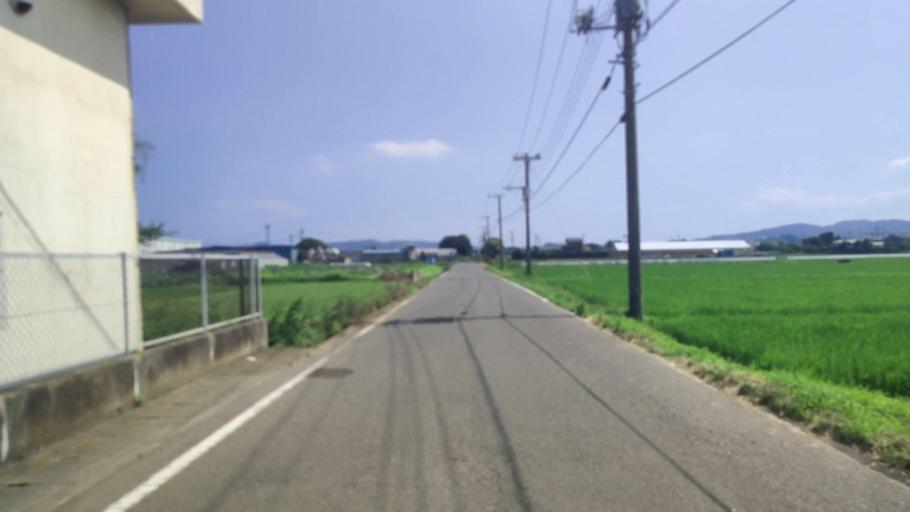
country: JP
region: Kanagawa
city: Isehara
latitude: 35.3698
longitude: 139.3073
